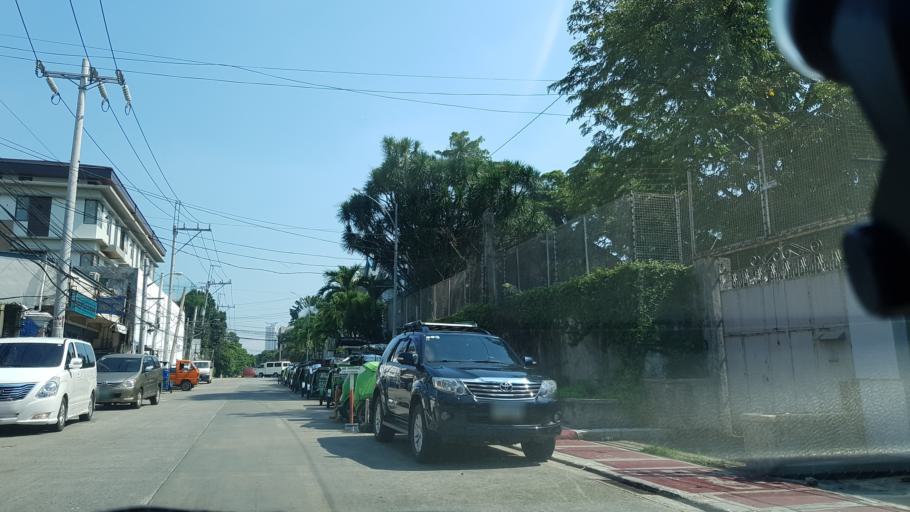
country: PH
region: Calabarzon
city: Del Monte
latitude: 14.6214
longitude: 121.0242
